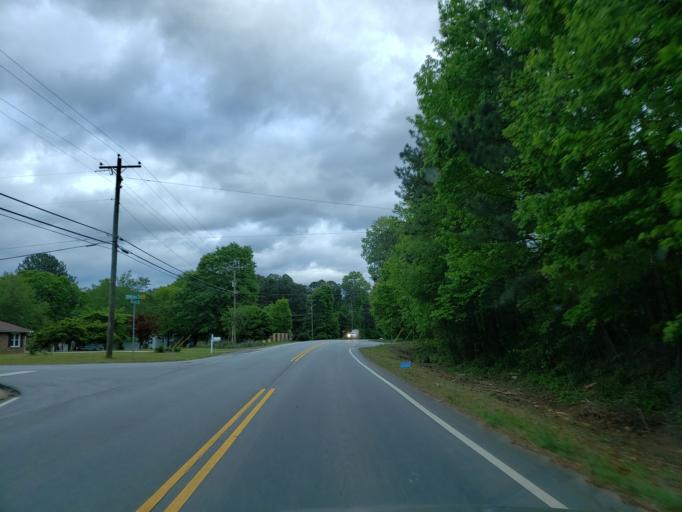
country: US
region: Georgia
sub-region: Paulding County
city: Dallas
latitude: 33.8729
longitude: -84.8547
